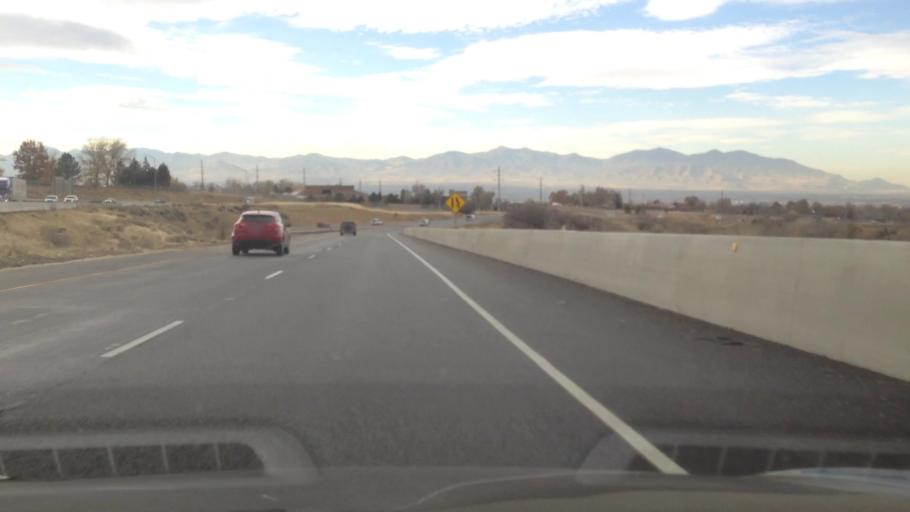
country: US
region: Utah
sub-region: Salt Lake County
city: Canyon Rim
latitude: 40.7142
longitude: -111.8161
